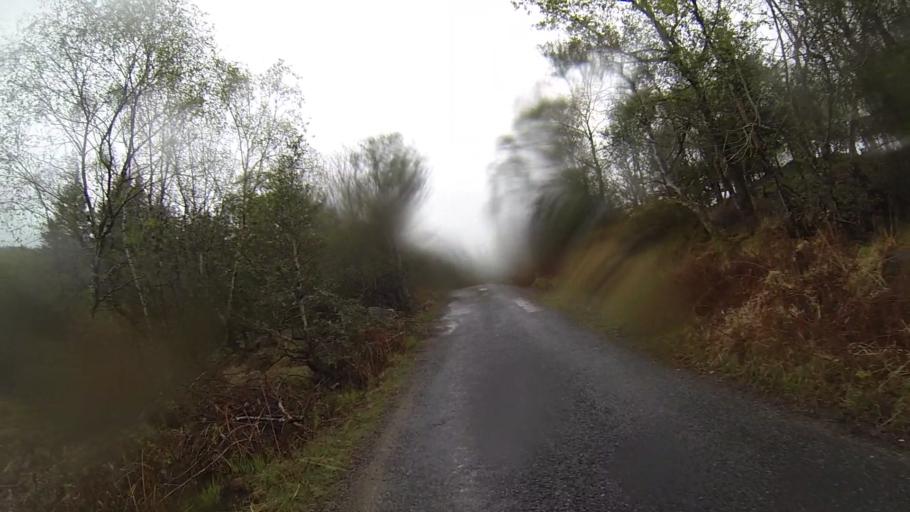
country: IE
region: Munster
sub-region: Ciarrai
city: Kenmare
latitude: 51.9653
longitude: -9.6349
